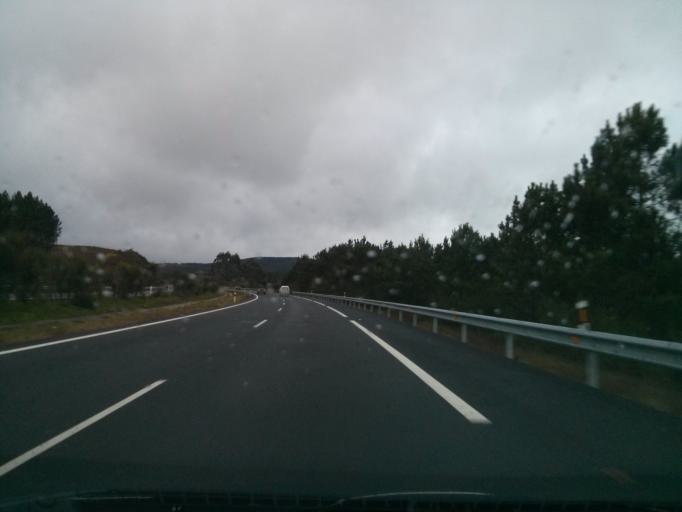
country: ES
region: Galicia
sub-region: Provincia de Pontevedra
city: Covelo
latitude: 42.2012
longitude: -8.2916
